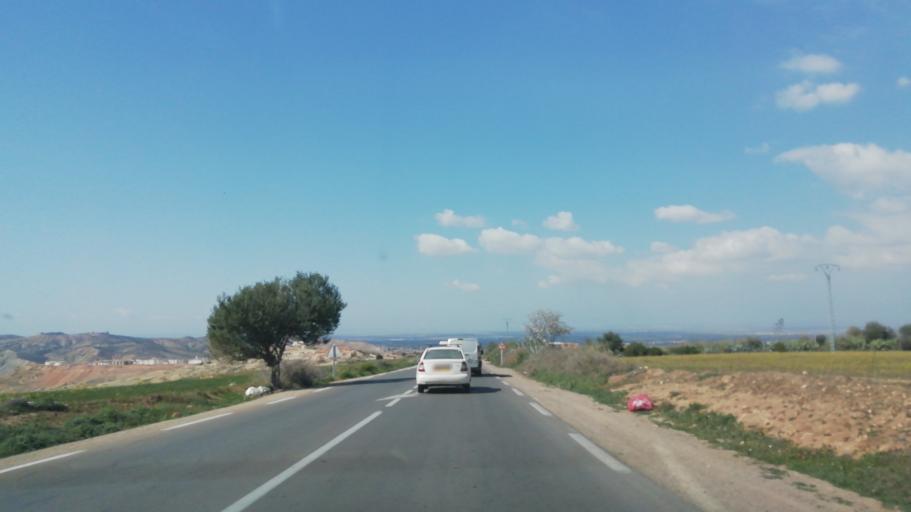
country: DZ
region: Mascara
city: Mascara
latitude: 35.5508
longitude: 0.0849
